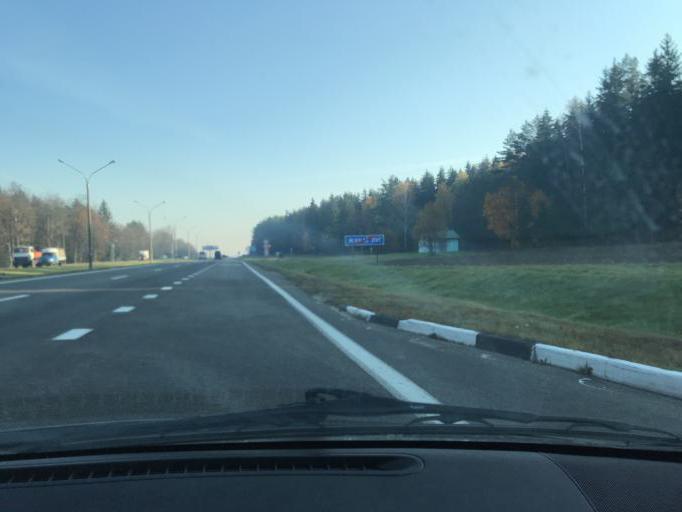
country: BY
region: Minsk
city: Korolev Stan
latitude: 53.9801
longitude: 27.7770
